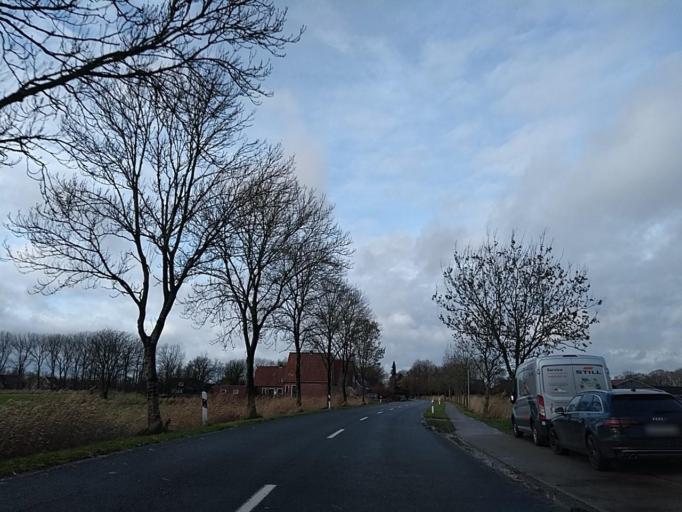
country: DE
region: Lower Saxony
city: Emden
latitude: 53.3176
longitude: 7.2637
